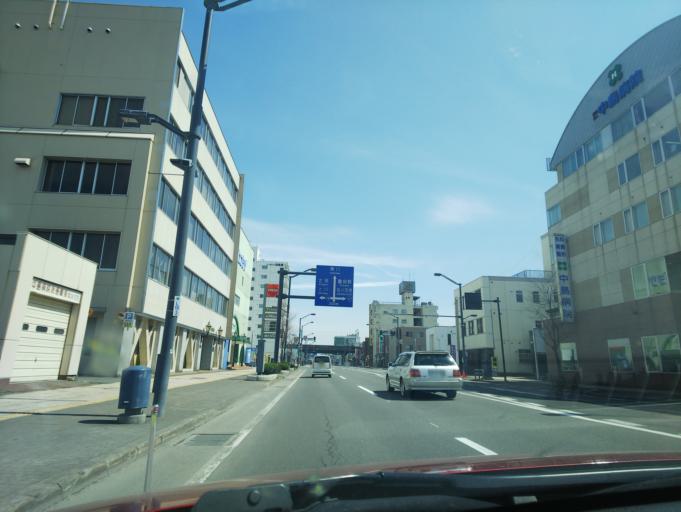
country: JP
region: Hokkaido
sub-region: Asahikawa-shi
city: Asahikawa
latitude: 43.7653
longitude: 142.3736
